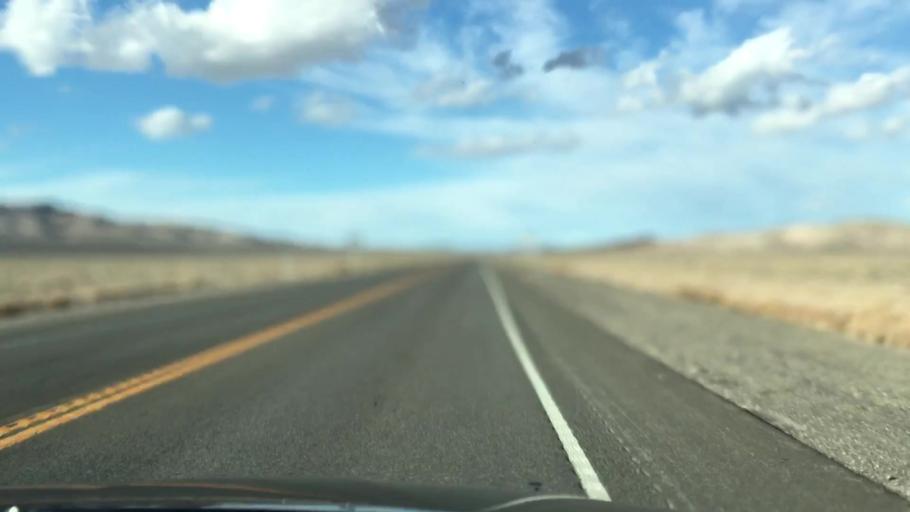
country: US
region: Nevada
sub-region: Esmeralda County
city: Goldfield
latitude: 37.5051
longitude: -117.1856
